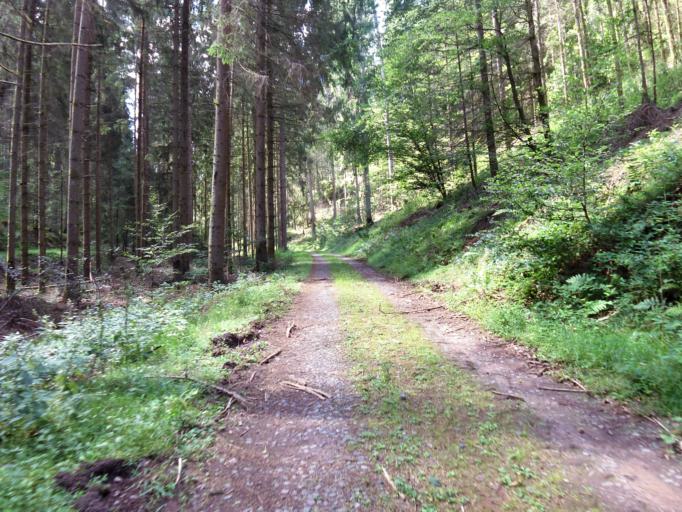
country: DE
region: Rheinland-Pfalz
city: Elmstein
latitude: 49.4062
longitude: 7.9282
